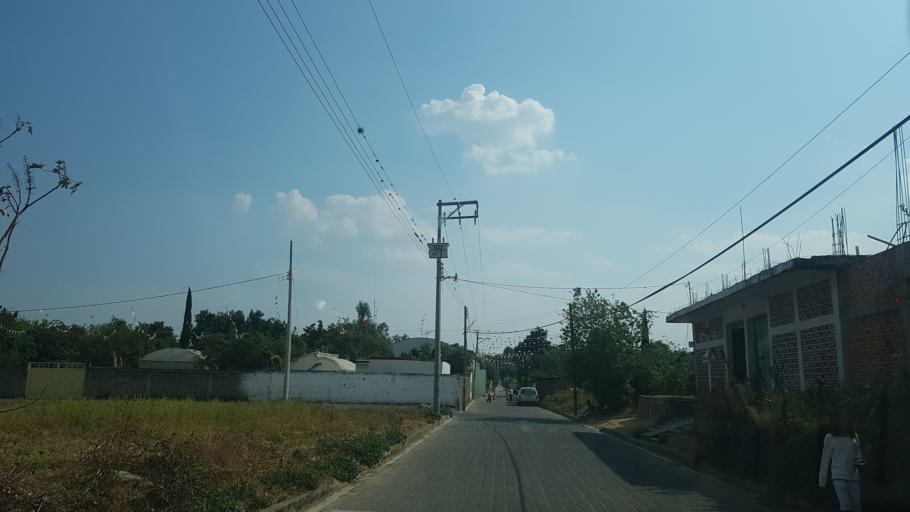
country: MX
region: Puebla
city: San Juan Amecac
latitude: 18.8213
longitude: -98.7054
